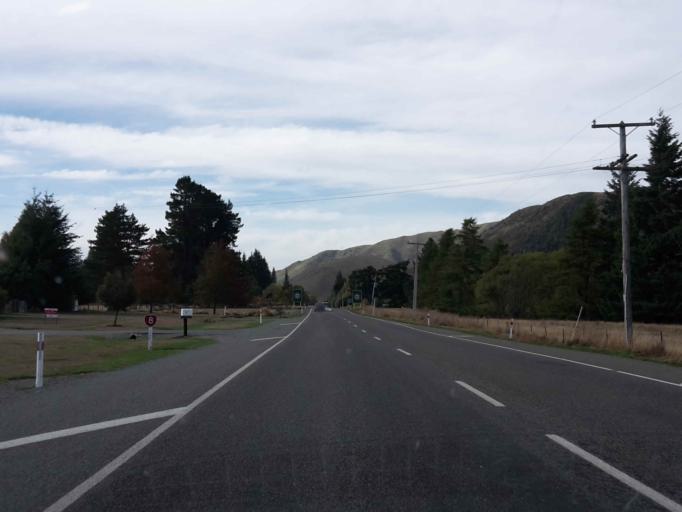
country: NZ
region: Canterbury
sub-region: Timaru District
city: Pleasant Point
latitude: -44.0887
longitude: 170.6535
